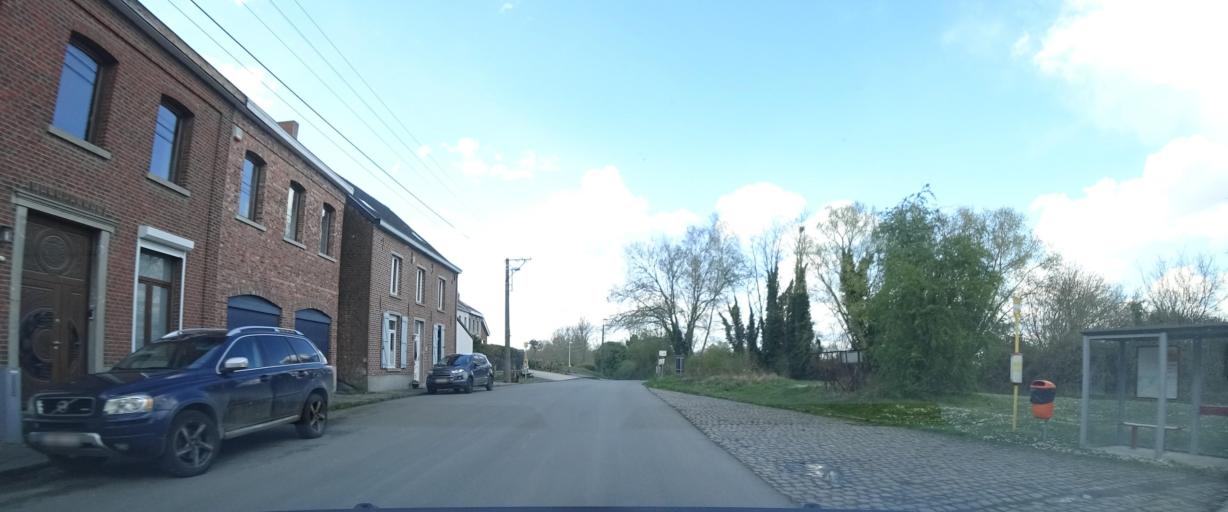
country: BE
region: Wallonia
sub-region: Province du Brabant Wallon
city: Rebecq-Rognon
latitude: 50.6518
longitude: 4.1065
